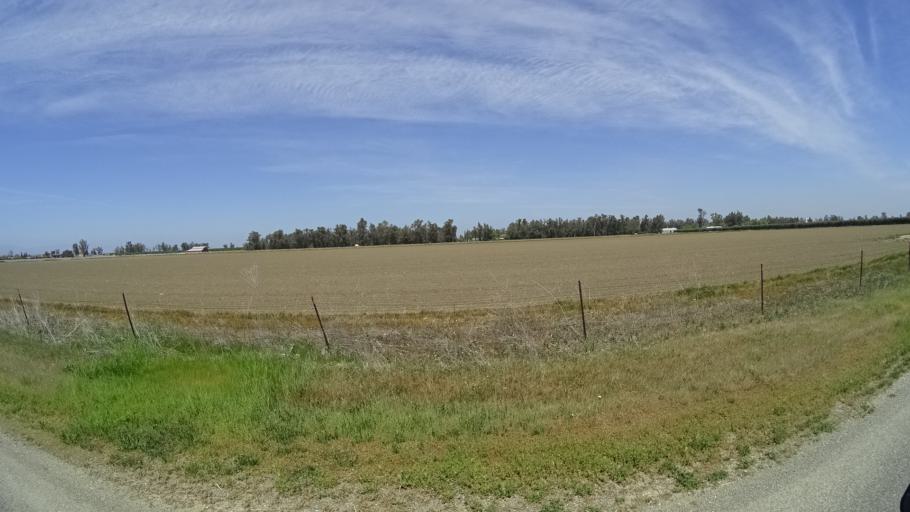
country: US
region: California
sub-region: Glenn County
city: Willows
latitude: 39.5763
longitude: -122.2012
